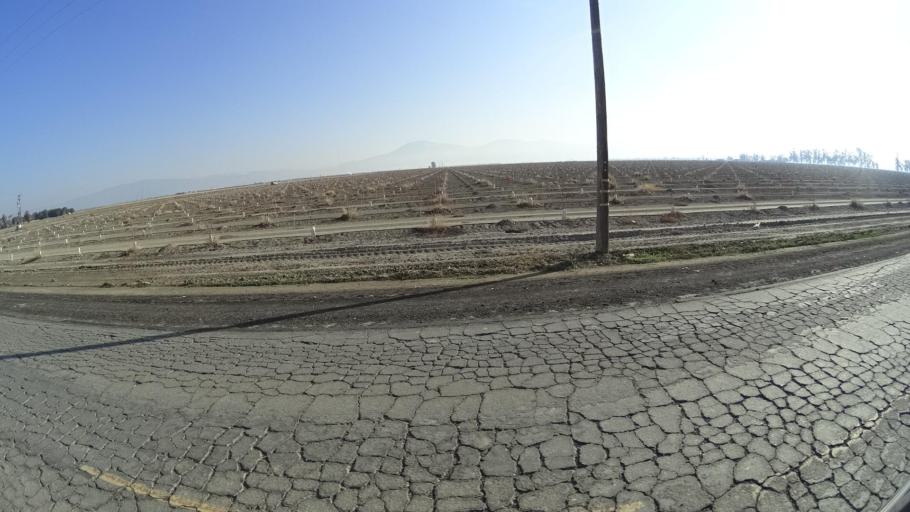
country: US
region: California
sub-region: Kern County
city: Weedpatch
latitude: 35.1936
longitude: -118.9681
